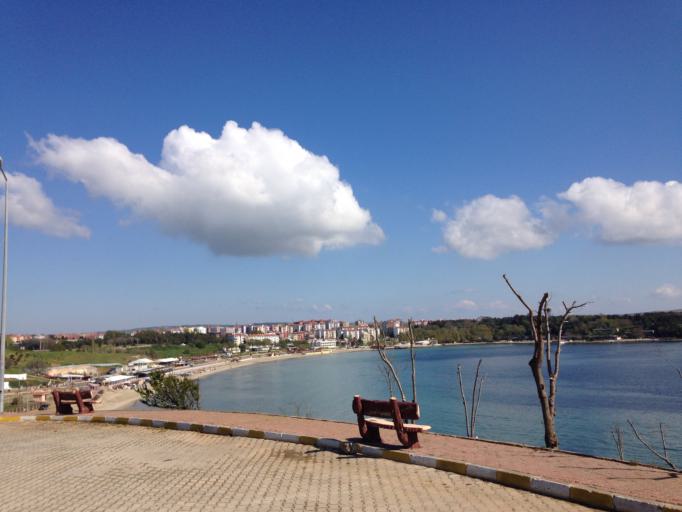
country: TR
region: Canakkale
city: Gelibolu
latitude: 40.4099
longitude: 26.6811
